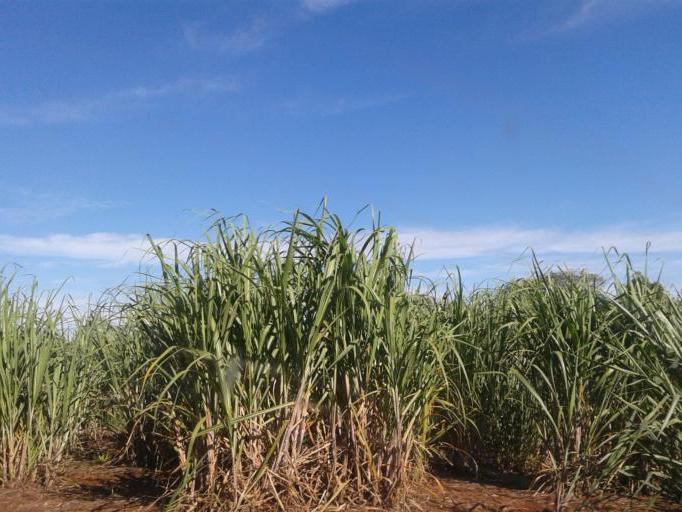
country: BR
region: Minas Gerais
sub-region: Capinopolis
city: Capinopolis
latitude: -18.6784
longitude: -49.6303
